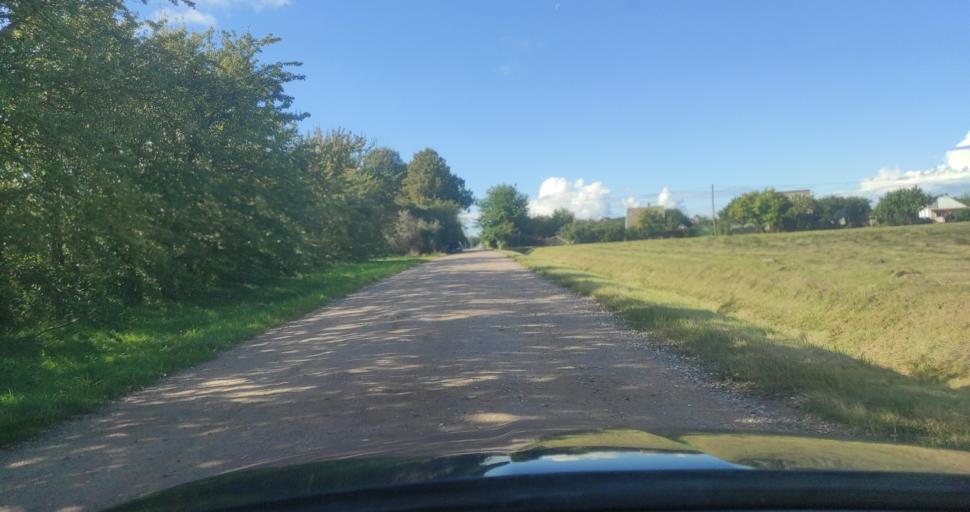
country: LV
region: Ventspils
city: Ventspils
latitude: 57.3660
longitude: 21.6080
